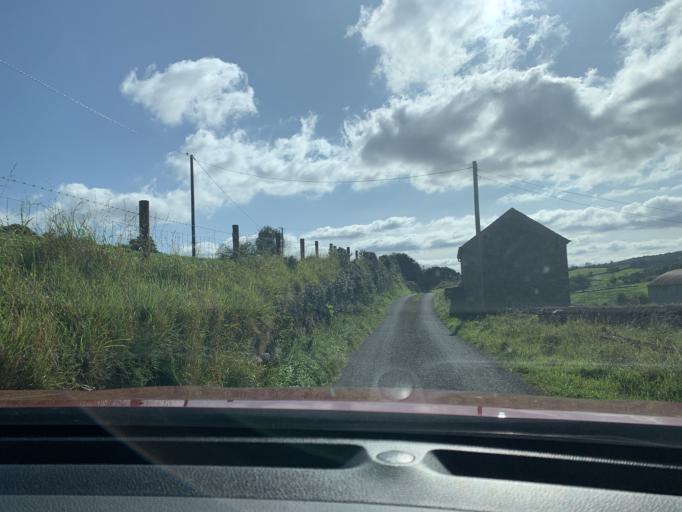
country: IE
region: Connaught
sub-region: Roscommon
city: Boyle
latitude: 54.0781
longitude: -8.3660
